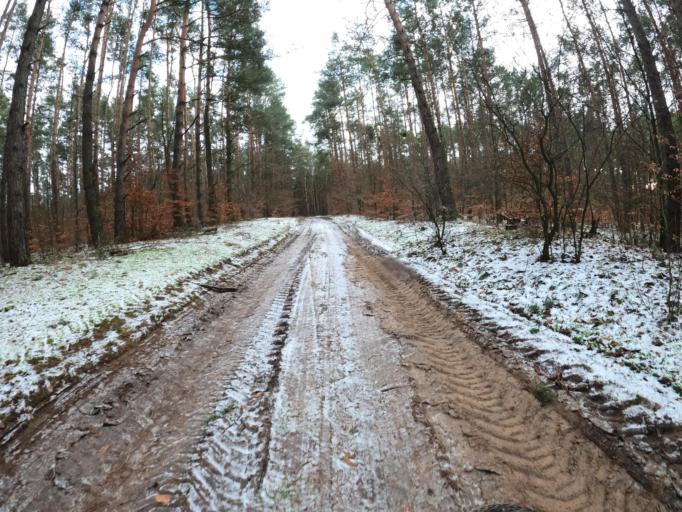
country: PL
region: Lubusz
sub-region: Powiat slubicki
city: Cybinka
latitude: 52.1949
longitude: 14.8631
